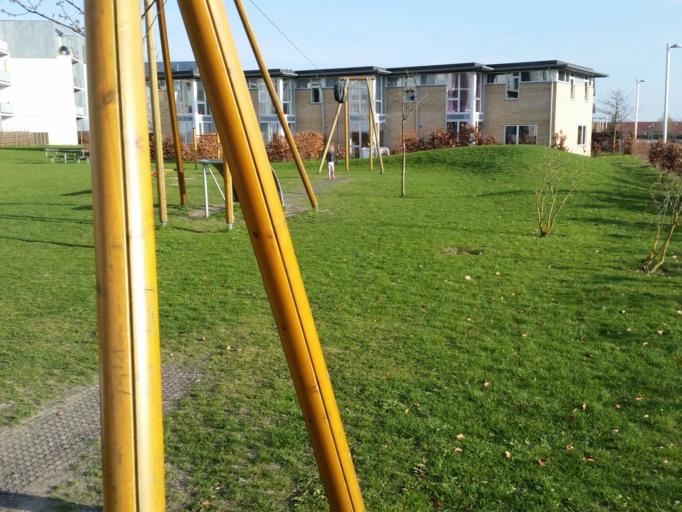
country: DK
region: Capital Region
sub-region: Albertslund Kommune
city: Albertslund
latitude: 55.6551
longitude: 12.3644
